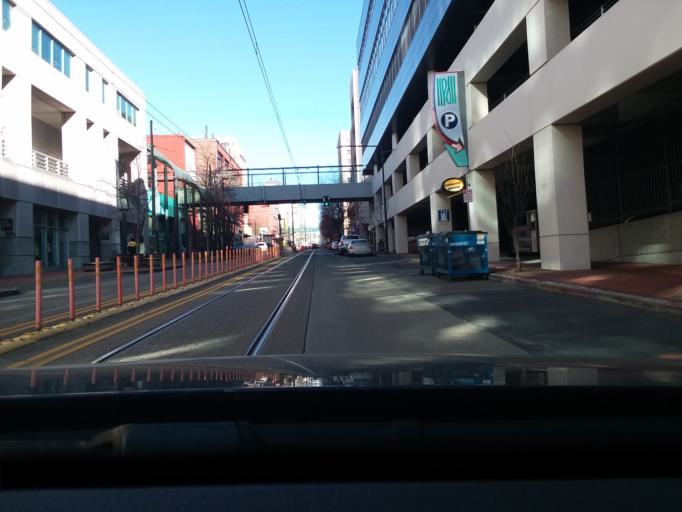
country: US
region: Washington
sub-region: Pierce County
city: Tacoma
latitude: 47.2514
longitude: -122.4390
